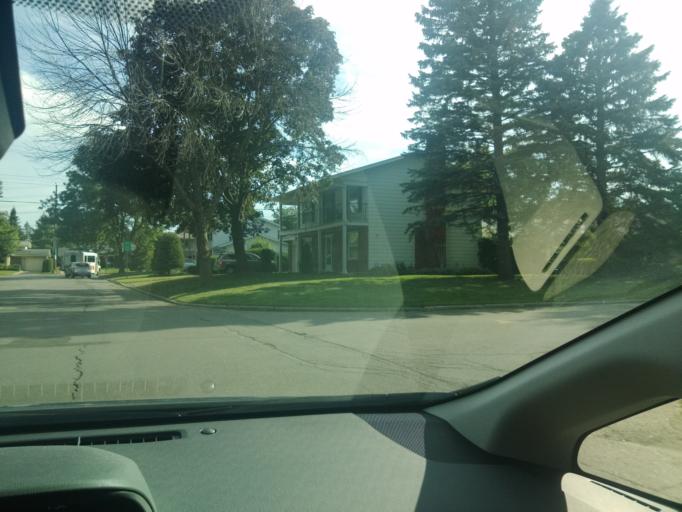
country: CA
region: Ontario
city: Ottawa
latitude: 45.3889
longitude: -75.6407
